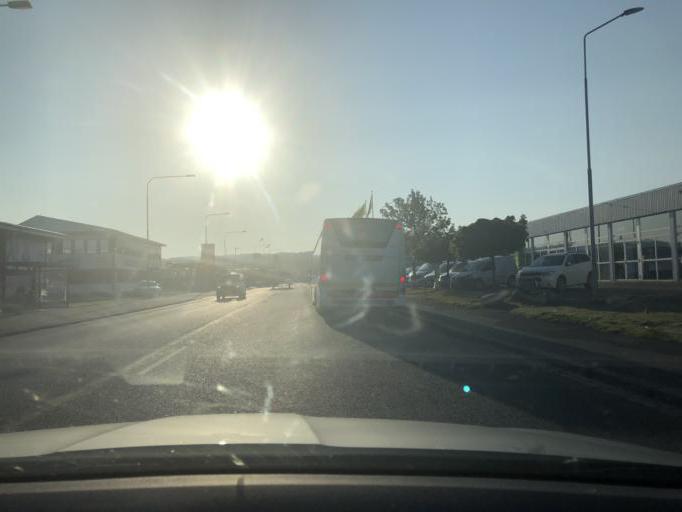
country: SE
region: Joenkoeping
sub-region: Jonkopings Kommun
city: Jonkoping
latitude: 57.7665
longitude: 14.1764
